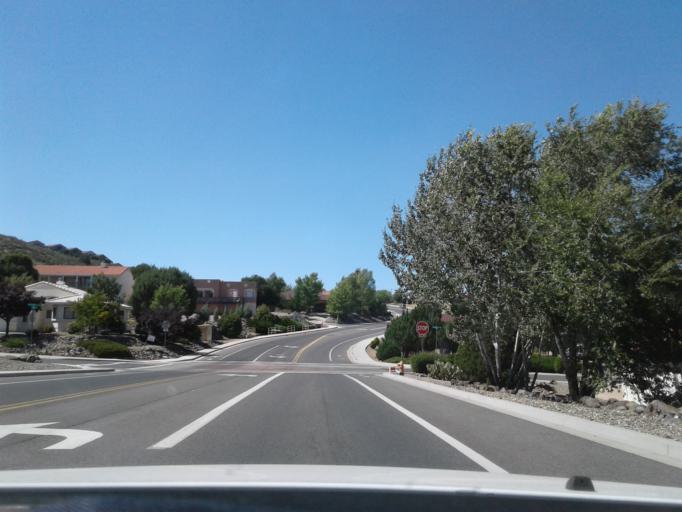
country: US
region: Arizona
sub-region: Yavapai County
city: Prescott
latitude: 34.5733
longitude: -112.4413
